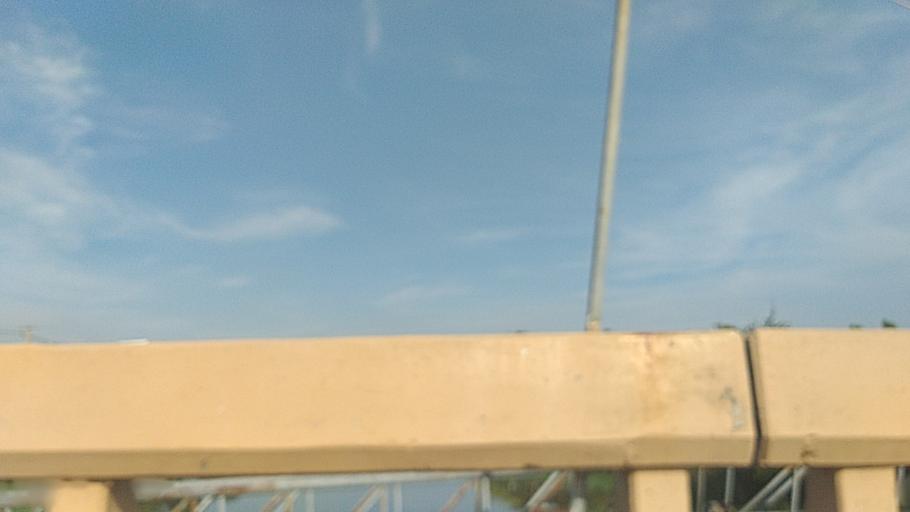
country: TH
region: Pathum Thani
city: Thanyaburi
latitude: 14.0238
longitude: 100.7442
